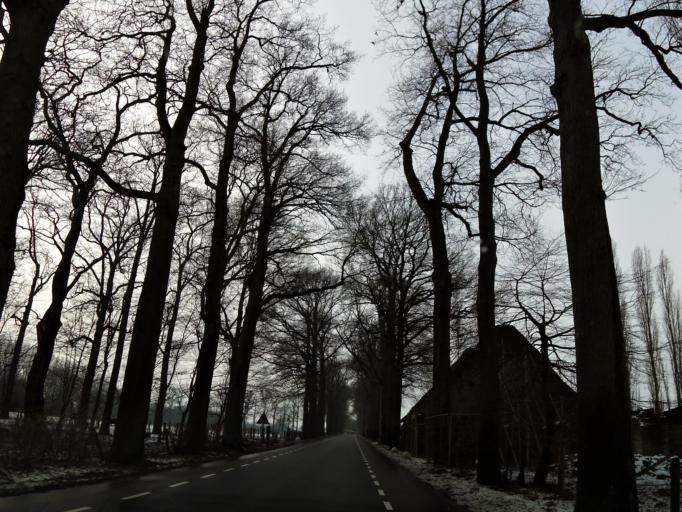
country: NL
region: Limburg
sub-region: Gemeente Voerendaal
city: Voerendaal
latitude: 50.8977
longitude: 5.9238
